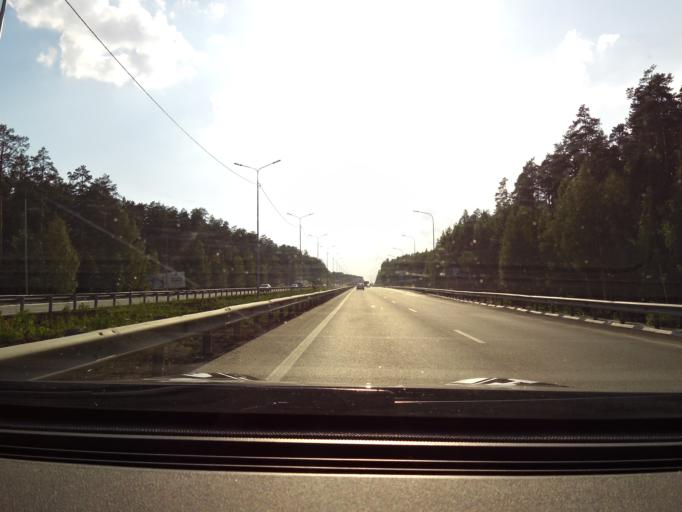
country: RU
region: Sverdlovsk
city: Shirokaya Rechka
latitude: 56.8255
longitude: 60.4742
